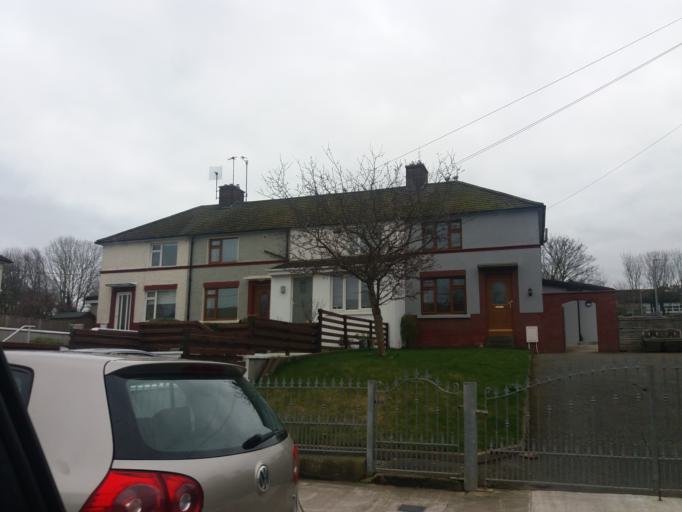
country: IE
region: Leinster
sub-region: Fingal County
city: Howth
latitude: 53.3855
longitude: -6.0698
